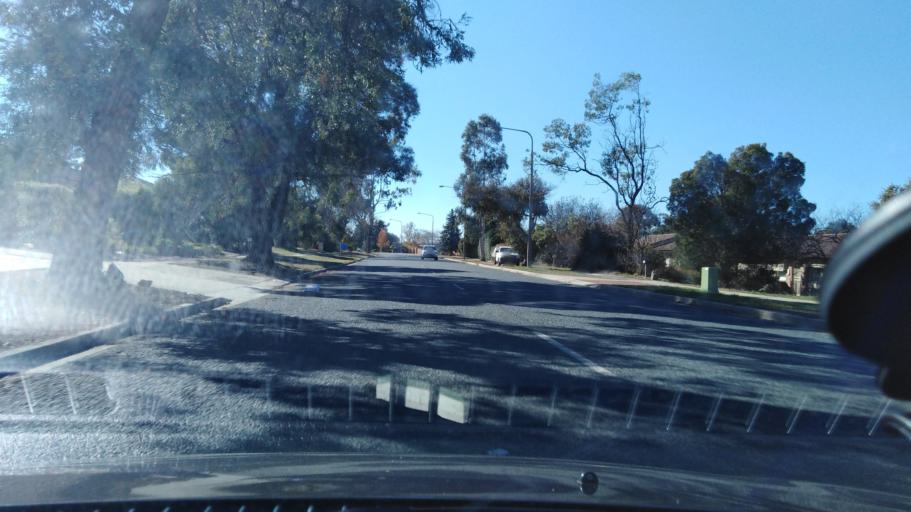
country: AU
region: Australian Capital Territory
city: Forrest
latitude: -35.3451
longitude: 149.0384
